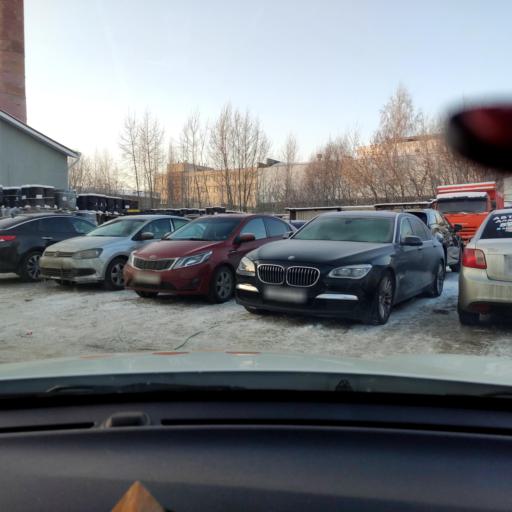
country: RU
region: Tatarstan
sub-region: Gorod Kazan'
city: Kazan
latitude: 55.7982
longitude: 49.0571
